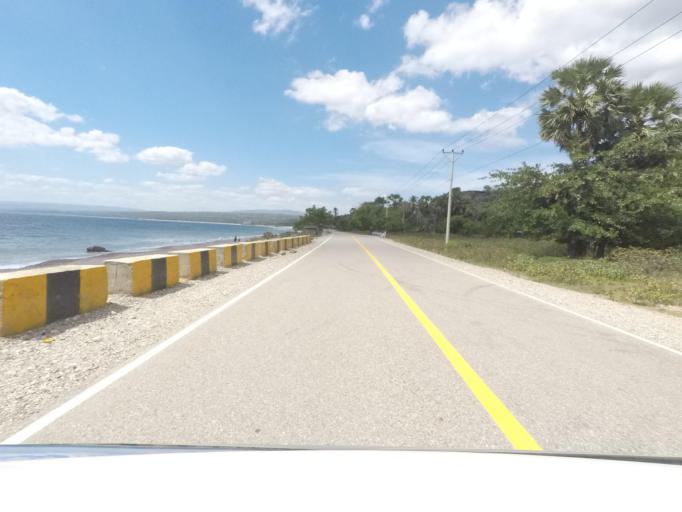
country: TL
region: Lautem
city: Lospalos
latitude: -8.4163
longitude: 126.7486
